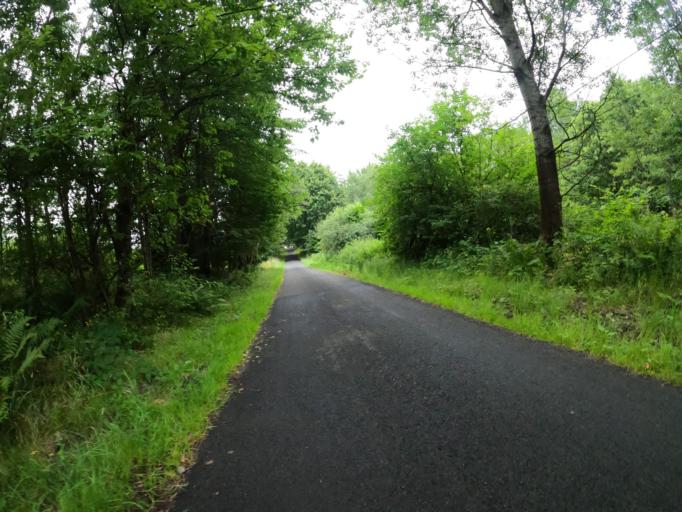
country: PL
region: West Pomeranian Voivodeship
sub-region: Powiat szczecinecki
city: Grzmiaca
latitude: 53.9556
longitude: 16.4624
